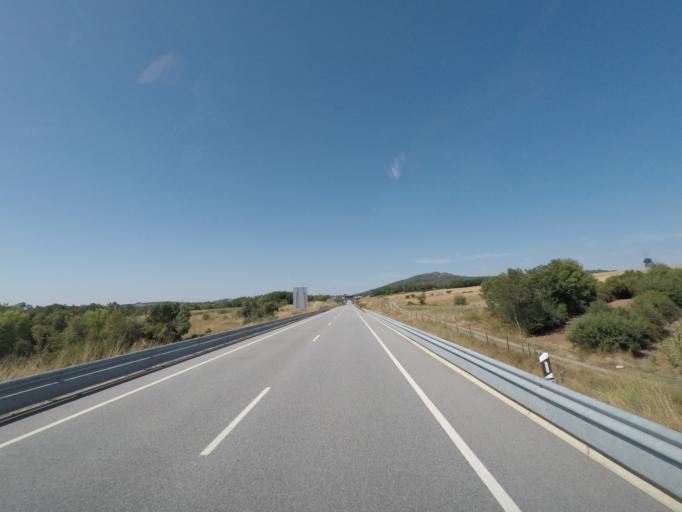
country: PT
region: Braganca
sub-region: Mogadouro
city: Mogadouro
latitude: 41.3545
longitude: -6.5859
